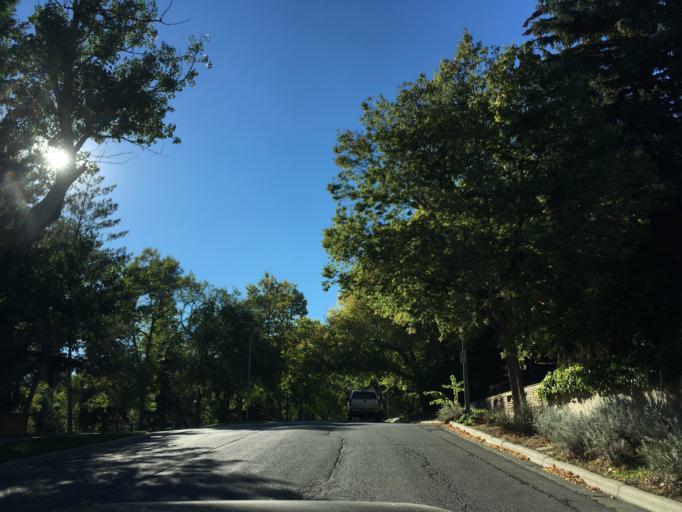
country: US
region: Montana
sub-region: Yellowstone County
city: Billings
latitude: 45.7900
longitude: -108.5225
